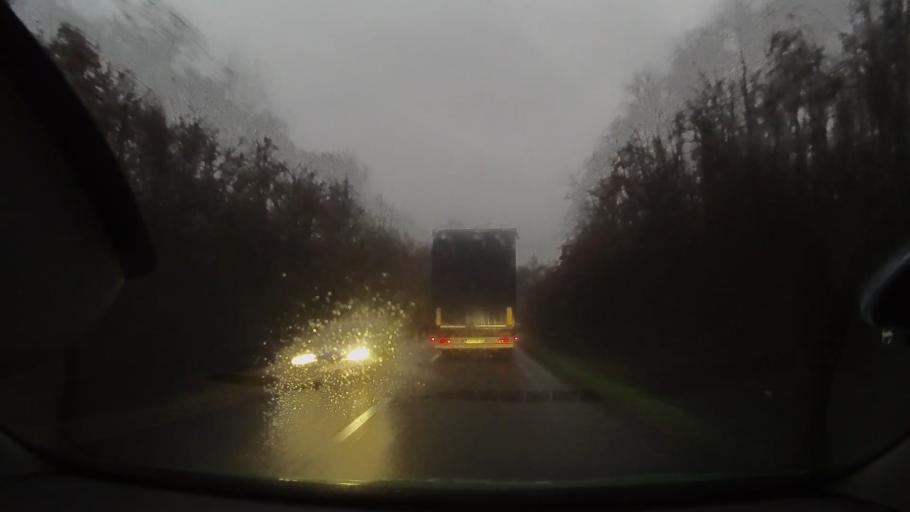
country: RO
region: Arad
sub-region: Comuna Beliu
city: Beliu
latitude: 46.5055
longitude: 21.9710
